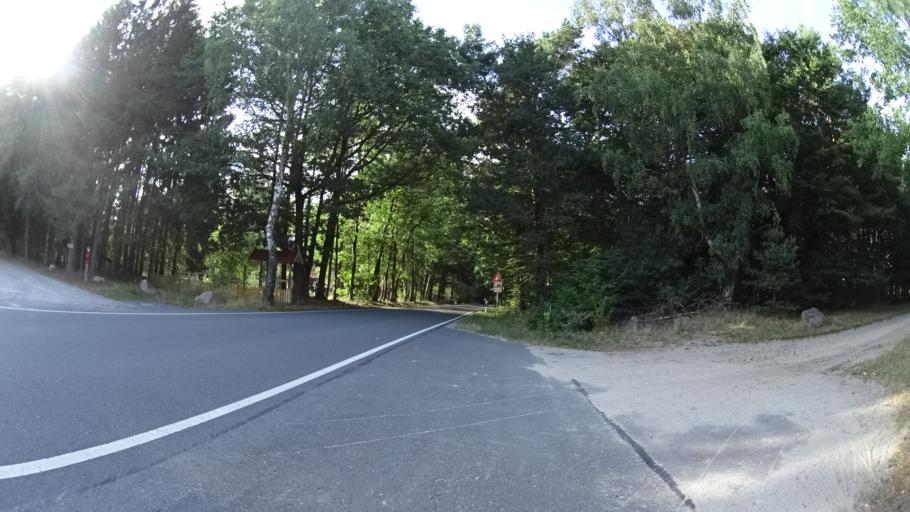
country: DE
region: Lower Saxony
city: Undeloh
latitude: 53.1532
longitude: 9.9067
